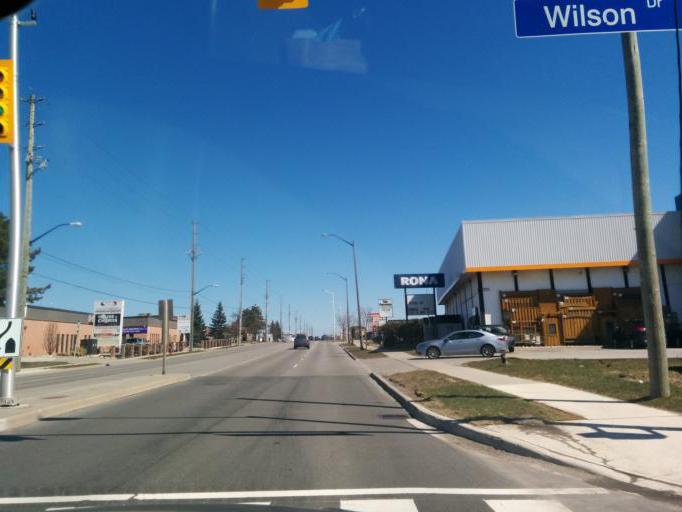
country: CA
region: Ontario
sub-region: Halton
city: Milton
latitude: 43.5230
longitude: -79.8724
